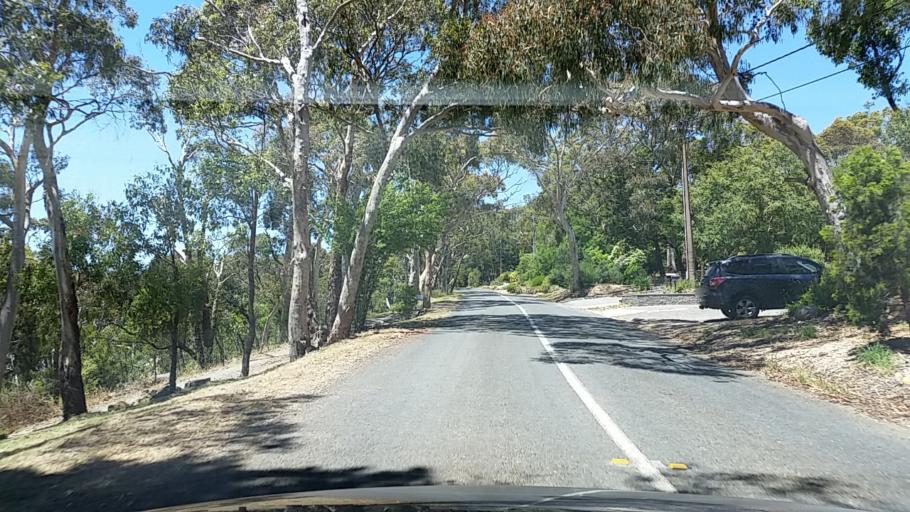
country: AU
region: South Australia
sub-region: Adelaide Hills
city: Crafers
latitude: -34.9999
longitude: 138.6851
